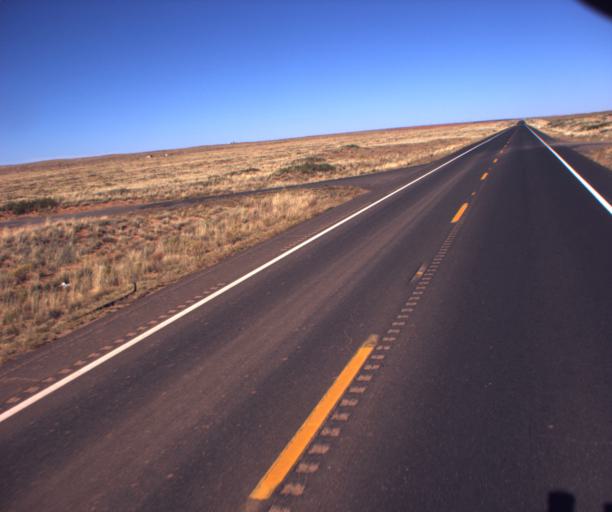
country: US
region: Arizona
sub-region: Coconino County
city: Kaibito
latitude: 36.3664
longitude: -110.8985
